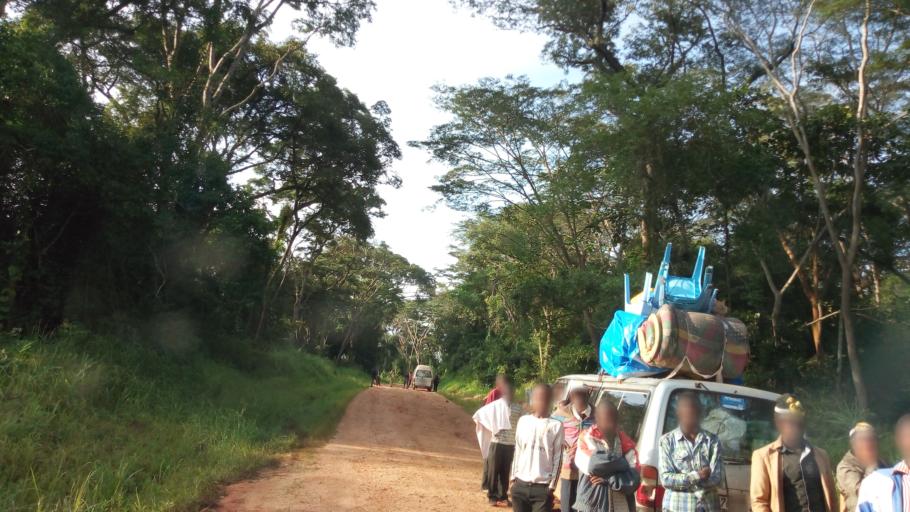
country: BI
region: Bururi
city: Rumonge
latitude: -4.4542
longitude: 28.8481
